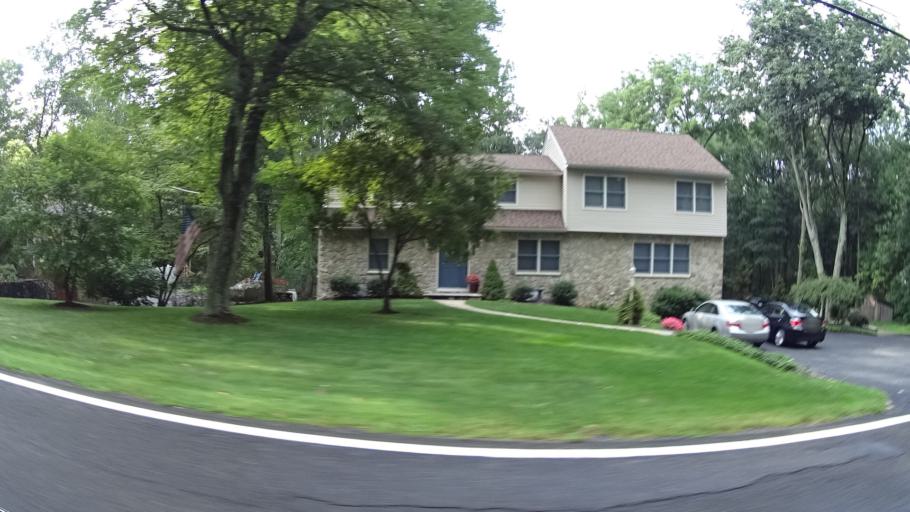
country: US
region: New Jersey
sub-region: Union County
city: Berkeley Heights
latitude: 40.6917
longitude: -74.4610
